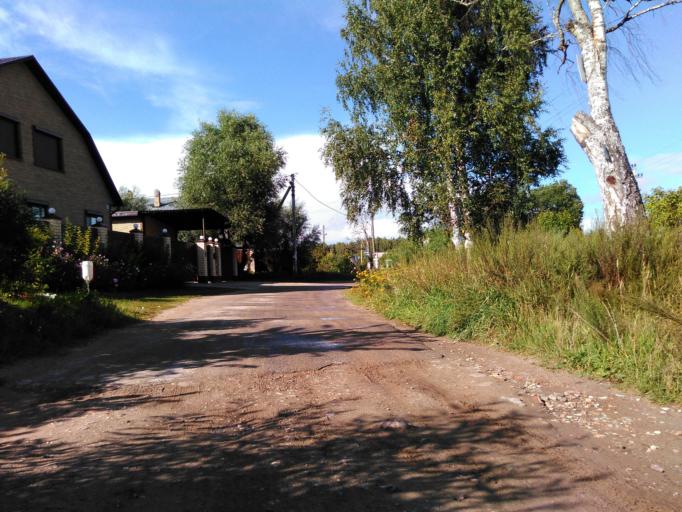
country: RU
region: Vladimir
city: Pokrov
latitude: 55.9760
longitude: 39.1198
